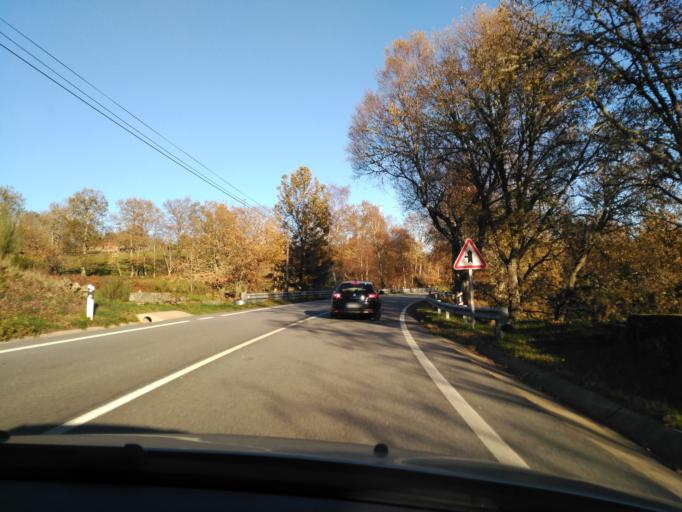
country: PT
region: Vila Real
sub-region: Montalegre
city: Montalegre
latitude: 41.7607
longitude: -7.8153
